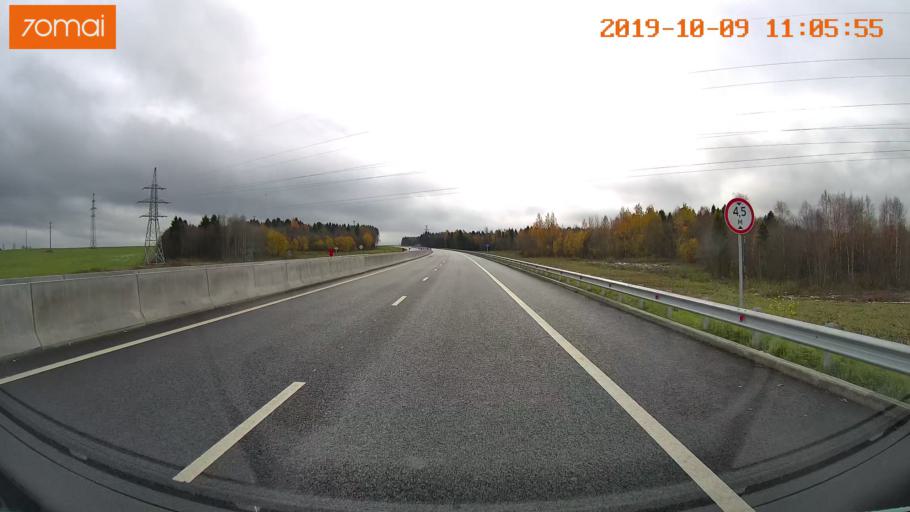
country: RU
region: Vologda
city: Molochnoye
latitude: 59.1932
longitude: 39.7581
